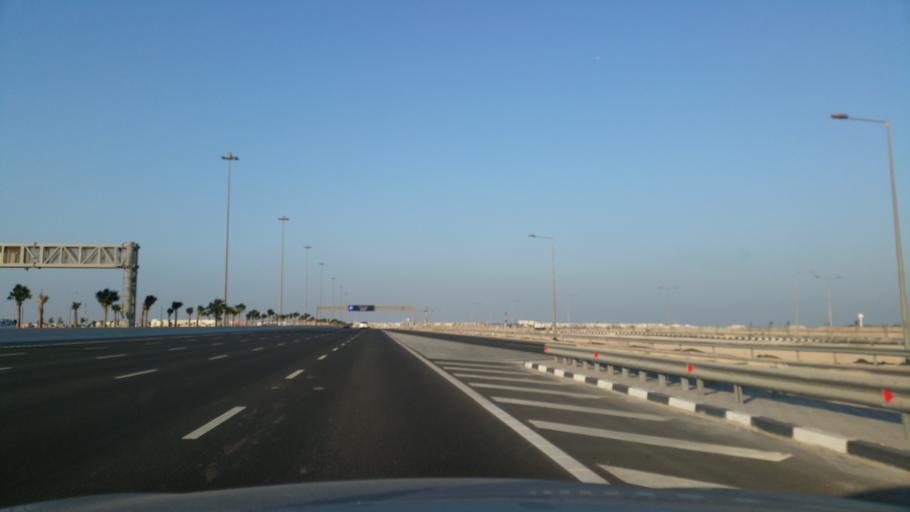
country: QA
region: Al Khawr
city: Al Khawr
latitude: 25.6500
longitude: 51.4966
